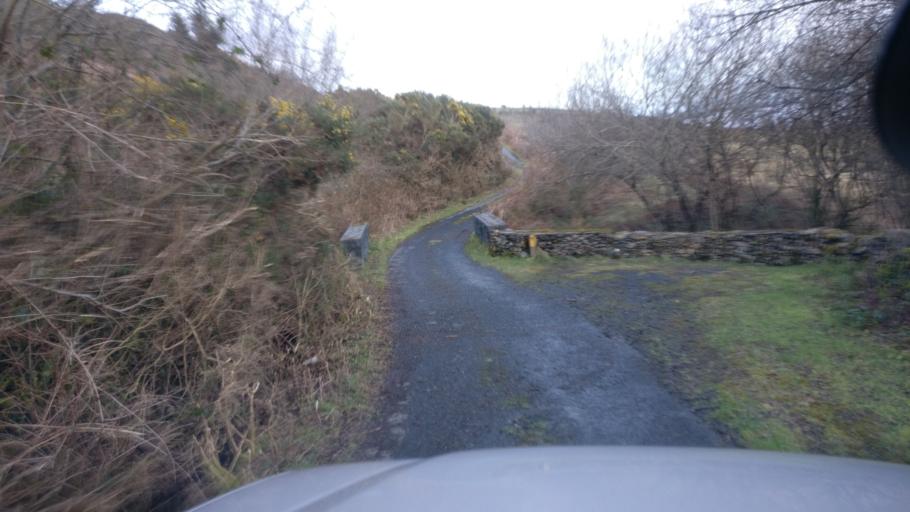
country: IE
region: Connaught
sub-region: County Galway
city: Oughterard
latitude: 53.5213
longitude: -9.4005
